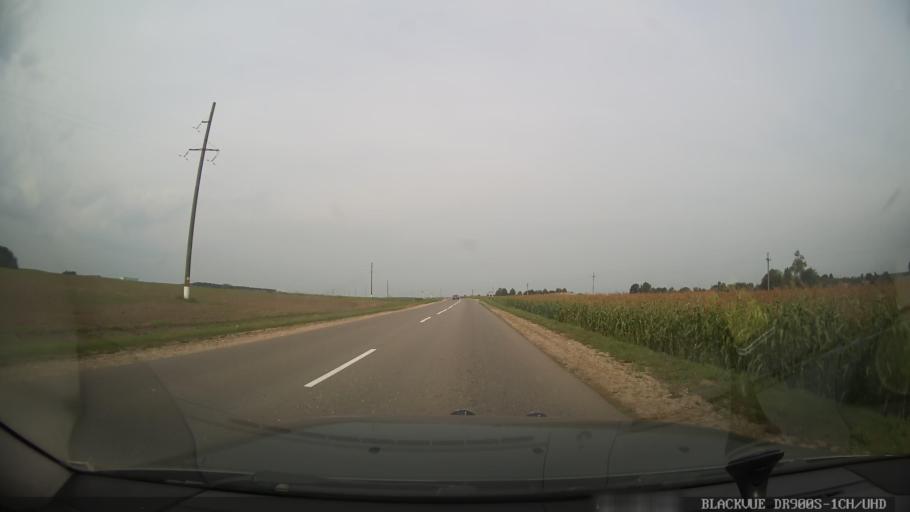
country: BY
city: Soly
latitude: 54.5634
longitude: 26.1035
